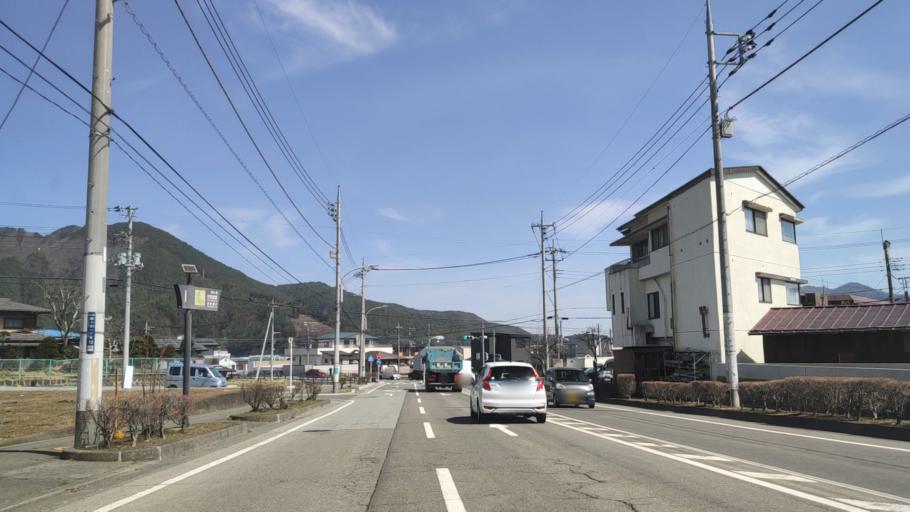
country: JP
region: Yamanashi
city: Fujikawaguchiko
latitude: 35.4904
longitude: 138.7926
